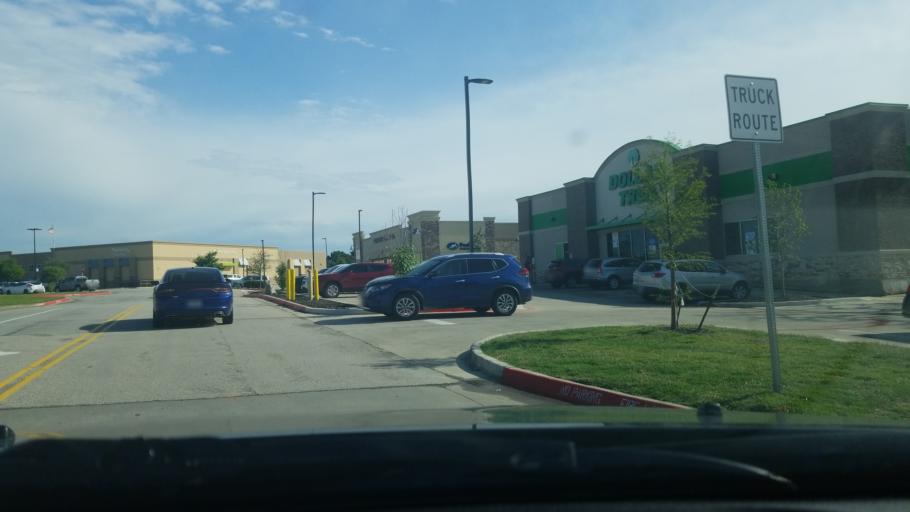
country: US
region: Texas
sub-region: Denton County
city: Corinth
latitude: 33.1613
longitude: -97.1076
